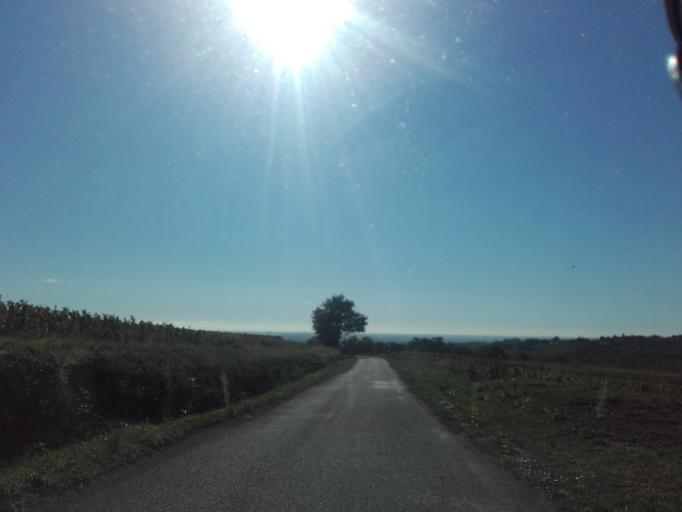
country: FR
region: Bourgogne
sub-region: Departement de Saone-et-Loire
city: Creches-sur-Saone
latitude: 46.2607
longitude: 4.7394
